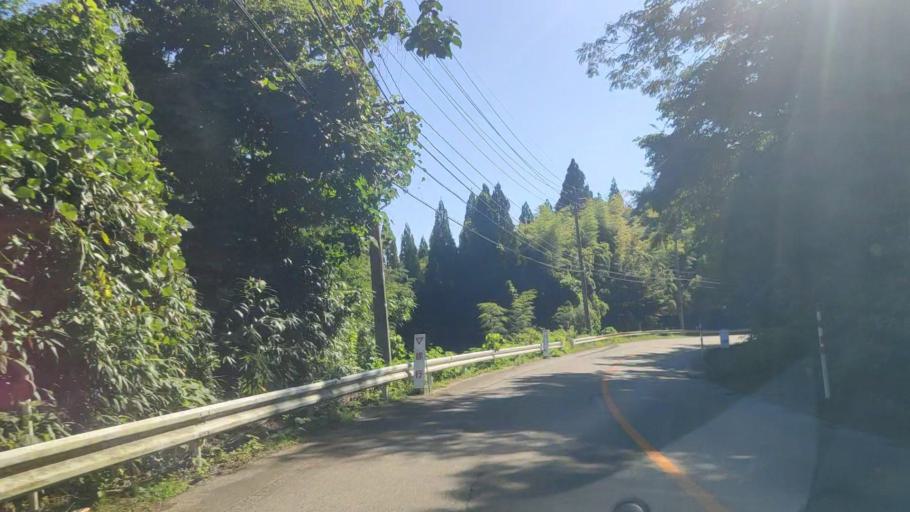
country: JP
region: Ishikawa
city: Nanao
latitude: 37.3418
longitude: 137.2295
